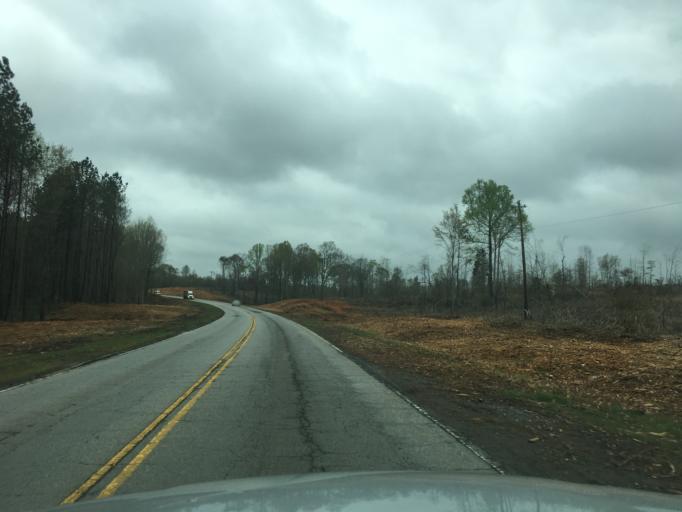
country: US
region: South Carolina
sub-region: Spartanburg County
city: Wellford
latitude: 34.9665
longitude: -82.0871
